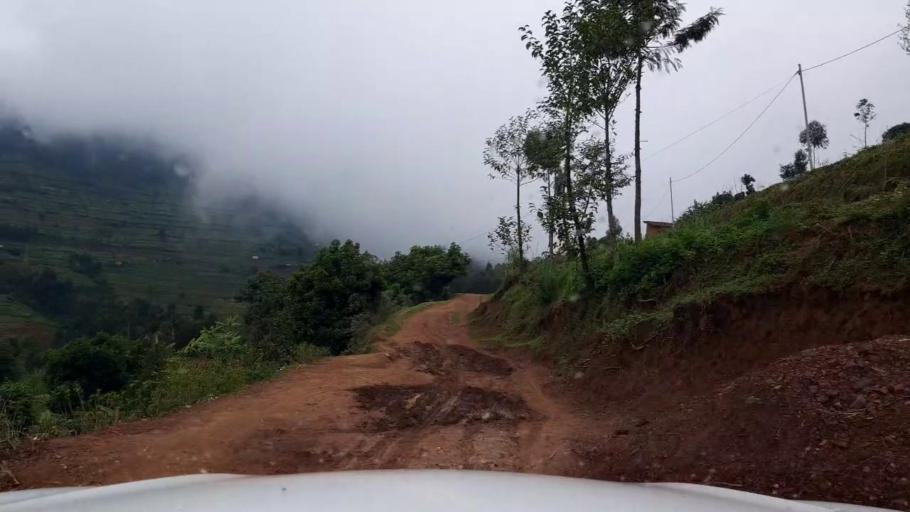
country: RW
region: Northern Province
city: Musanze
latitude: -1.5952
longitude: 29.7892
